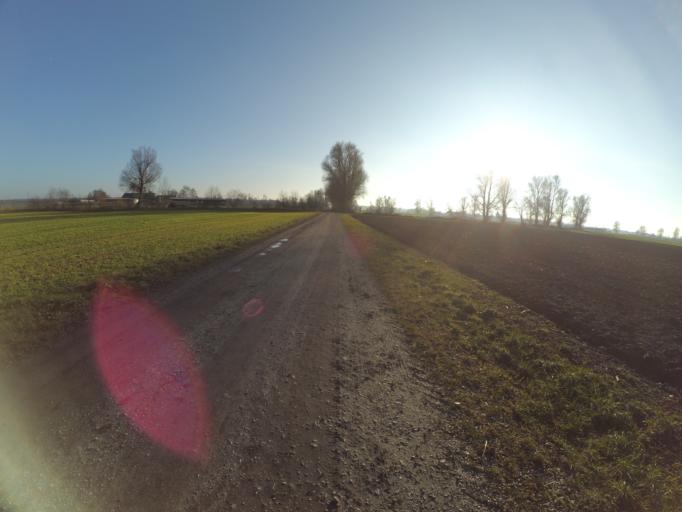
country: DE
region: Bavaria
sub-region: Swabia
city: Leipheim
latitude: 48.4711
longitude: 10.2080
